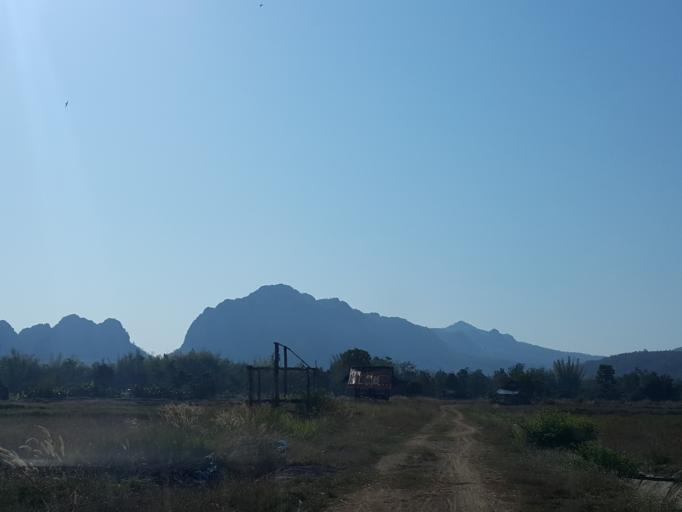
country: TH
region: Sukhothai
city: Thung Saliam
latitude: 17.3160
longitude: 99.4350
